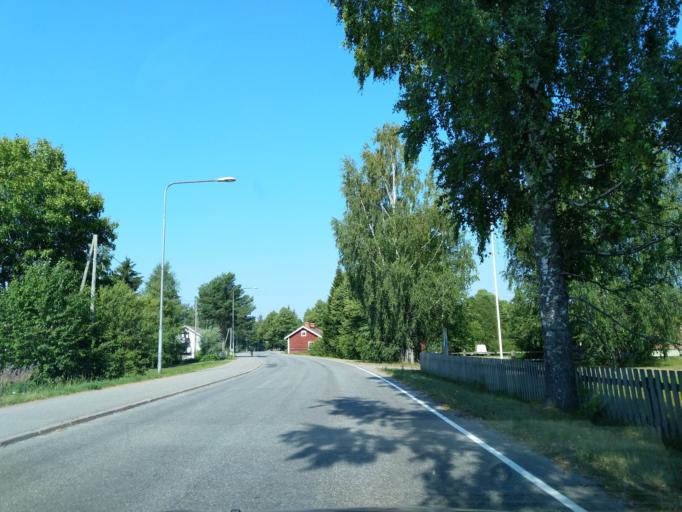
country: FI
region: Satakunta
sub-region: Pori
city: Noormarkku
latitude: 61.5906
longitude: 21.8841
